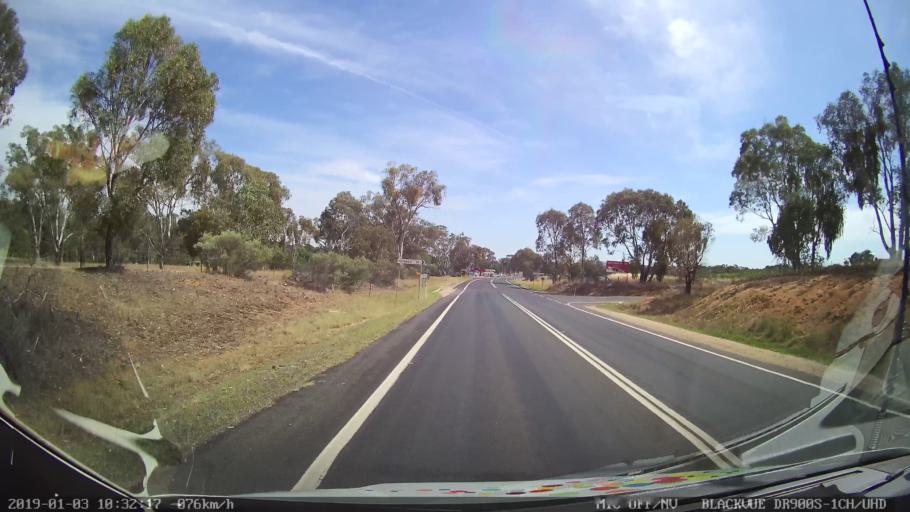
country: AU
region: New South Wales
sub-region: Young
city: Young
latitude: -34.3406
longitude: 148.2828
